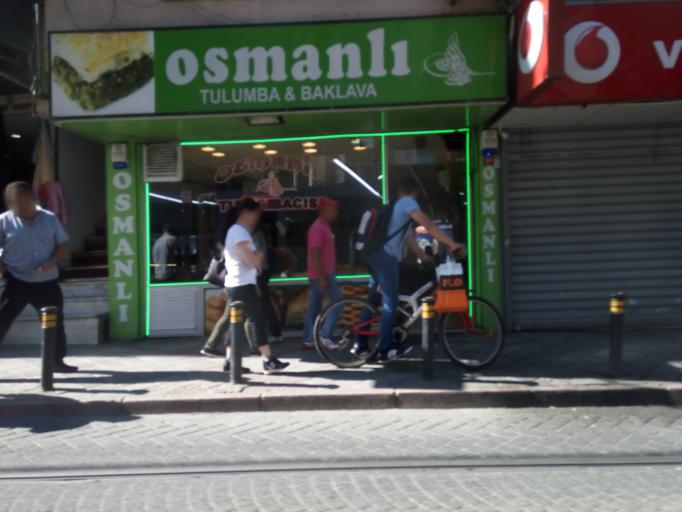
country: TR
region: Istanbul
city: Zeytinburnu
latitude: 41.0039
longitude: 28.9035
